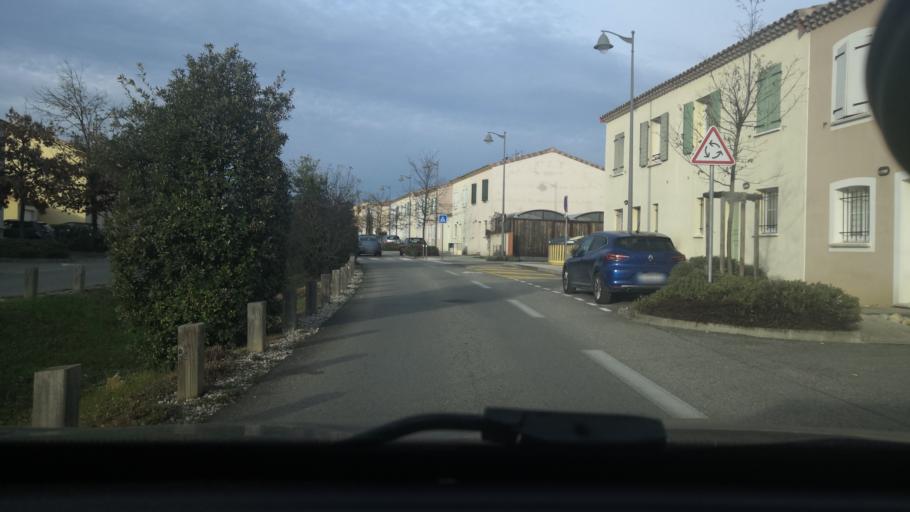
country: FR
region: Rhone-Alpes
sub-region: Departement de la Drome
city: Montelimar
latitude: 44.5360
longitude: 4.7681
